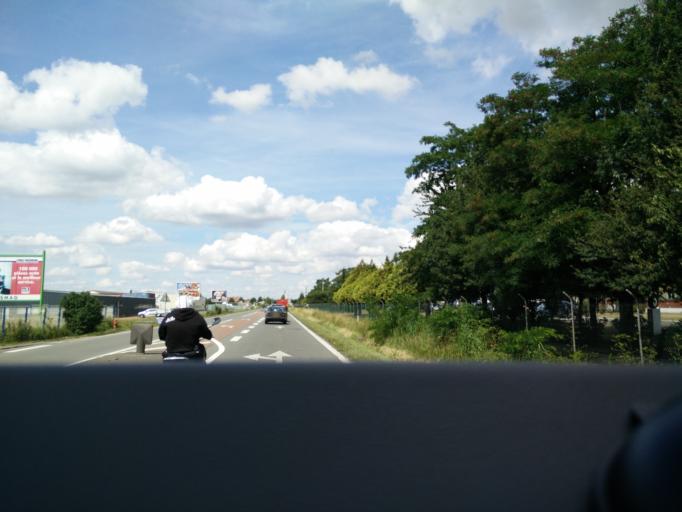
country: FR
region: Nord-Pas-de-Calais
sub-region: Departement du Pas-de-Calais
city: Essars
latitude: 50.5389
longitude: 2.6575
